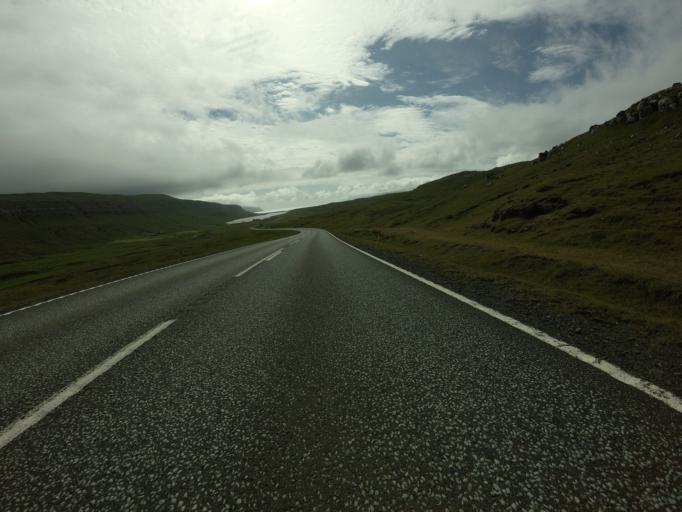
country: FO
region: Sandoy
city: Sandur
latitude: 61.8687
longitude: -6.8444
